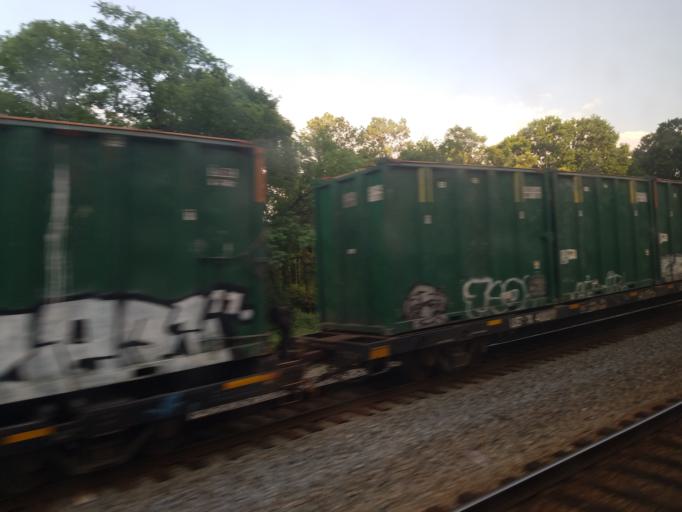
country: US
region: Washington, D.C.
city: Washington, D.C.
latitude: 38.8555
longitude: -77.0479
